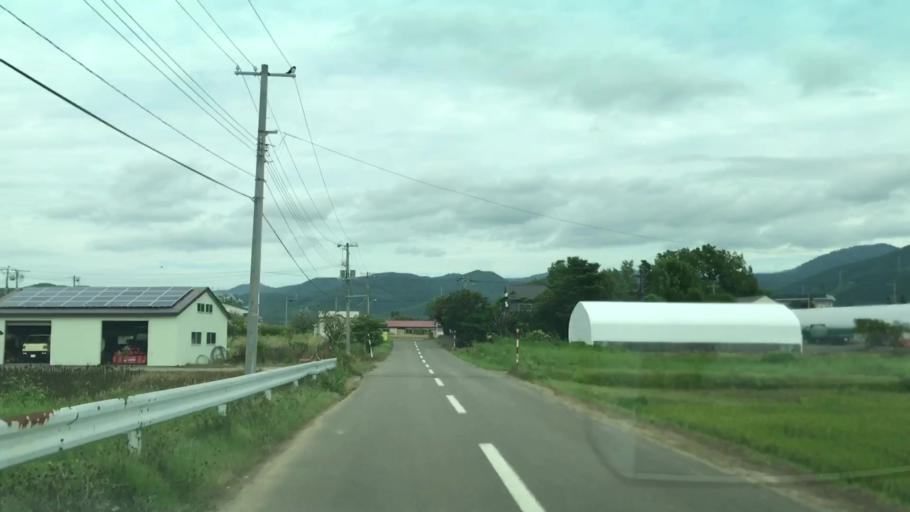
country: JP
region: Hokkaido
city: Iwanai
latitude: 43.0280
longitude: 140.5674
